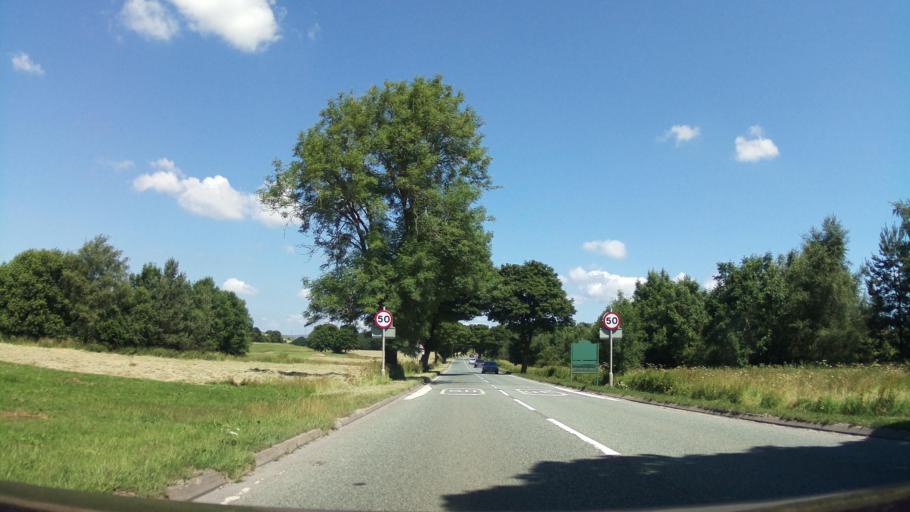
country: GB
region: England
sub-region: Derbyshire
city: Buxton
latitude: 53.2648
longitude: -1.8991
